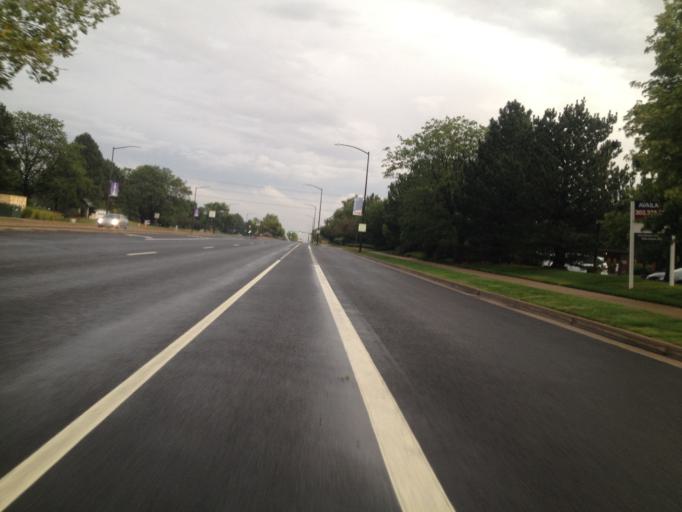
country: US
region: Colorado
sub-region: Boulder County
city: Louisville
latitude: 39.9868
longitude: -105.1585
